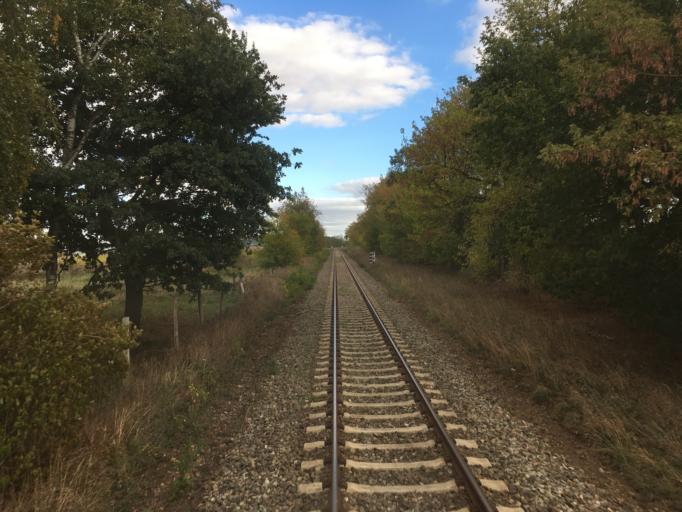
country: DE
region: Mecklenburg-Vorpommern
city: Grabowhofe
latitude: 53.5403
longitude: 12.5977
